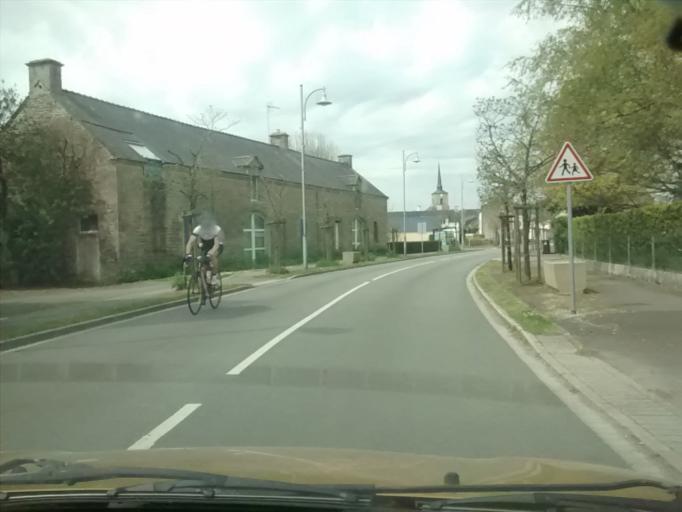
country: FR
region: Brittany
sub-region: Departement du Morbihan
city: Berric
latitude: 47.6325
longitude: -2.5217
